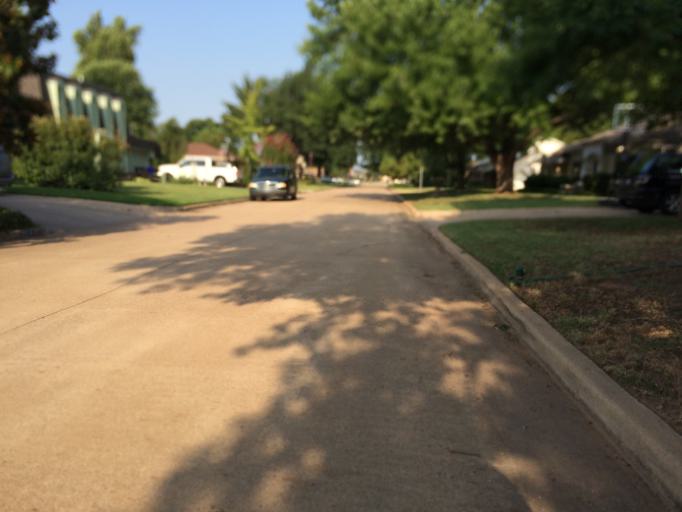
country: US
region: Oklahoma
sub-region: Cleveland County
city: Norman
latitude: 35.2261
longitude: -97.4739
